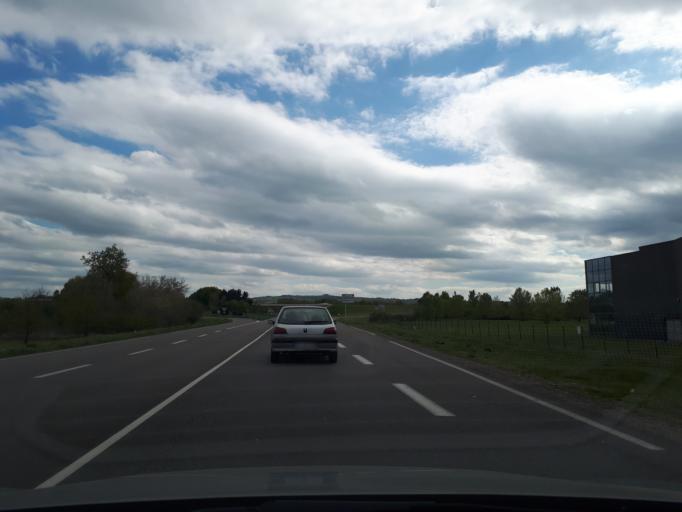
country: FR
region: Rhone-Alpes
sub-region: Departement de la Loire
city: Saint-Bonnet-les-Oules
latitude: 45.5405
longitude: 4.3055
